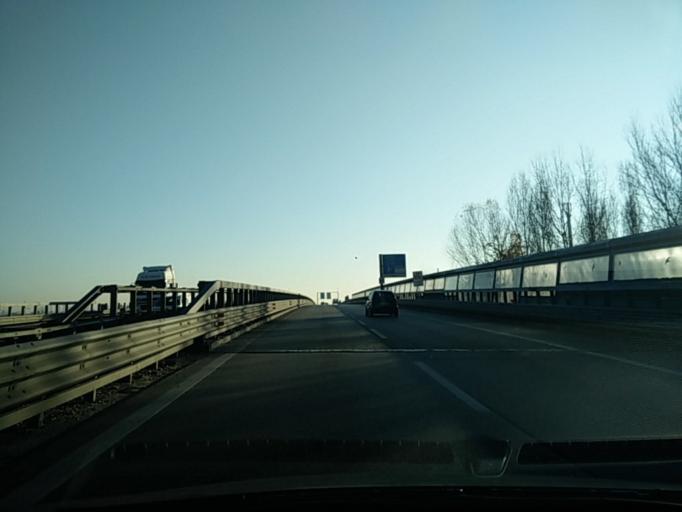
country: IT
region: Veneto
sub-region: Provincia di Padova
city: Vigodarzere
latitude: 45.4415
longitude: 11.8827
